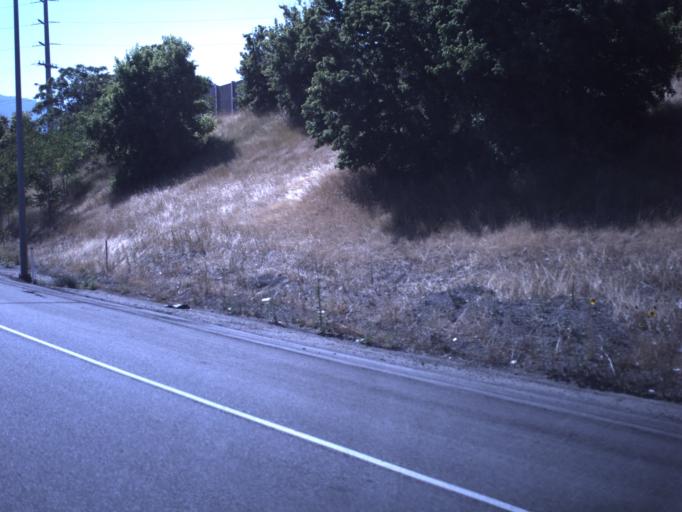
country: US
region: Utah
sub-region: Salt Lake County
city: Midvale
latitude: 40.6340
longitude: -111.8945
